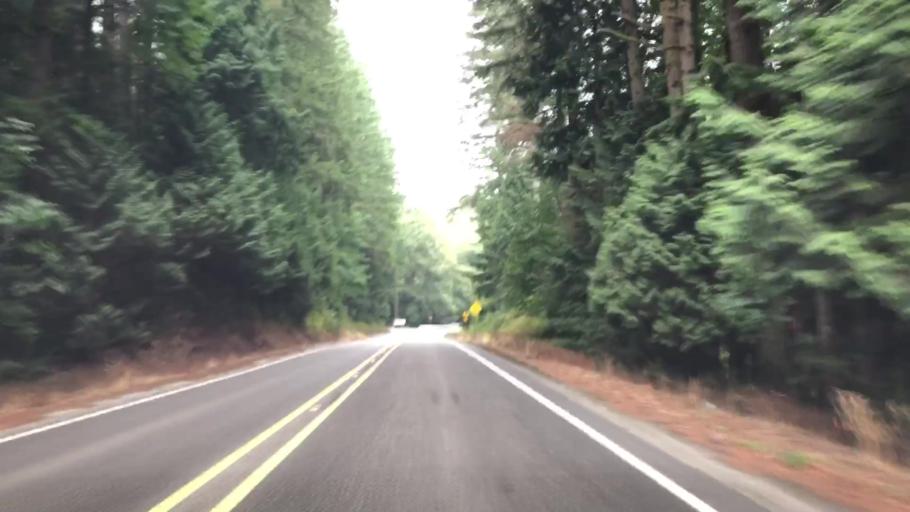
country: US
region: Washington
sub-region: Kitsap County
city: Navy Yard City
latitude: 47.5251
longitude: -122.7417
